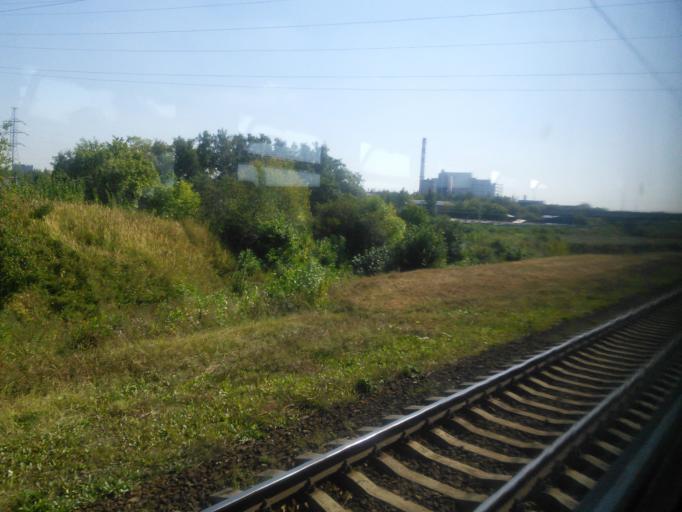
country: RU
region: Moskovskaya
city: Biryulevo Zapadnoye
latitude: 55.6068
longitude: 37.6358
